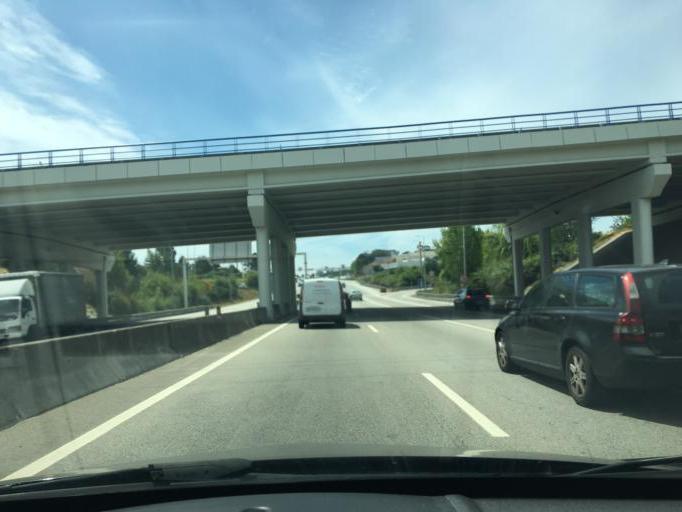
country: PT
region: Porto
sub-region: Maia
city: Leca do Bailio
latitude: 41.2033
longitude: -8.6275
